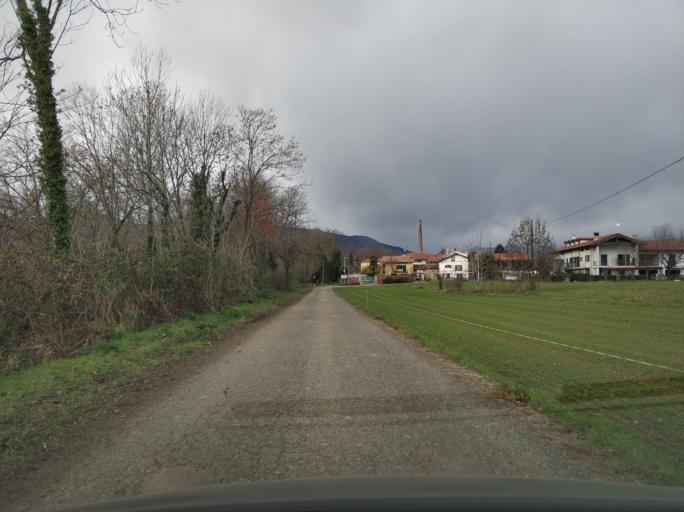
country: IT
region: Piedmont
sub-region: Provincia di Torino
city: Nole
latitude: 45.2255
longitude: 7.5786
